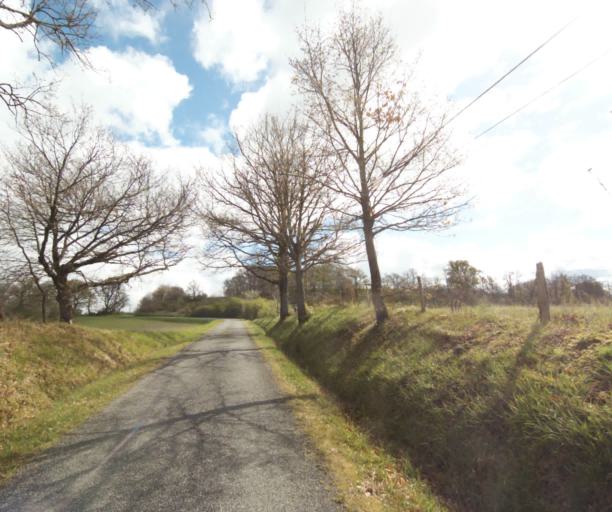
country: FR
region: Midi-Pyrenees
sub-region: Departement de l'Ariege
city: Saverdun
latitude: 43.2263
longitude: 1.5218
